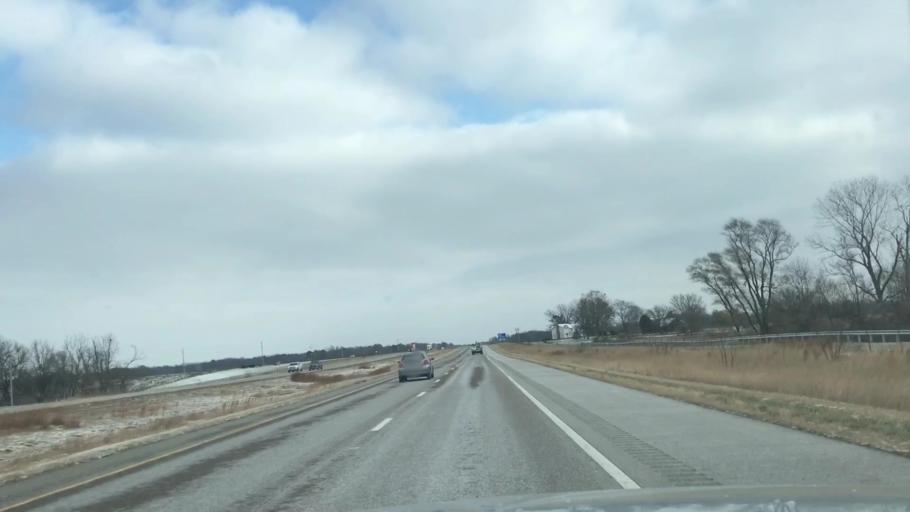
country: US
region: Illinois
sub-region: Madison County
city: Worden
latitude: 38.9469
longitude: -89.7805
